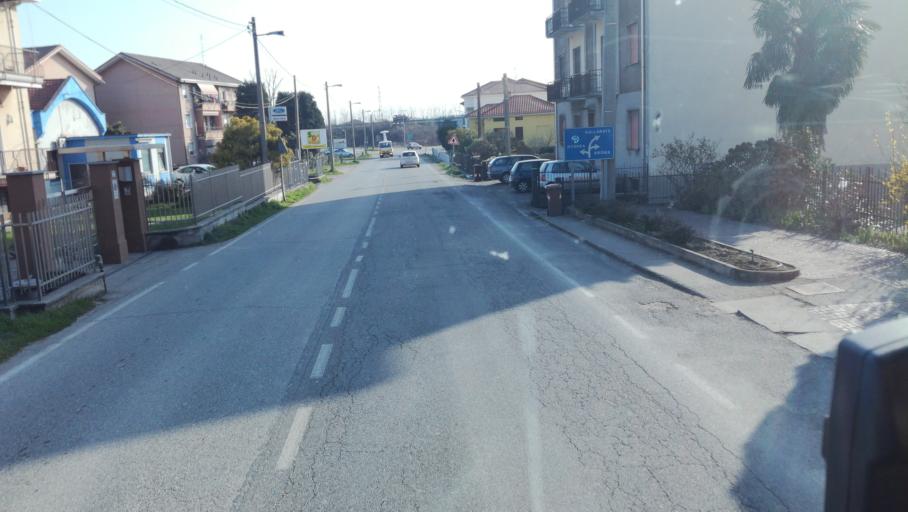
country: IT
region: Piedmont
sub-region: Provincia di Novara
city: Oleggio
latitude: 45.5934
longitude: 8.6419
